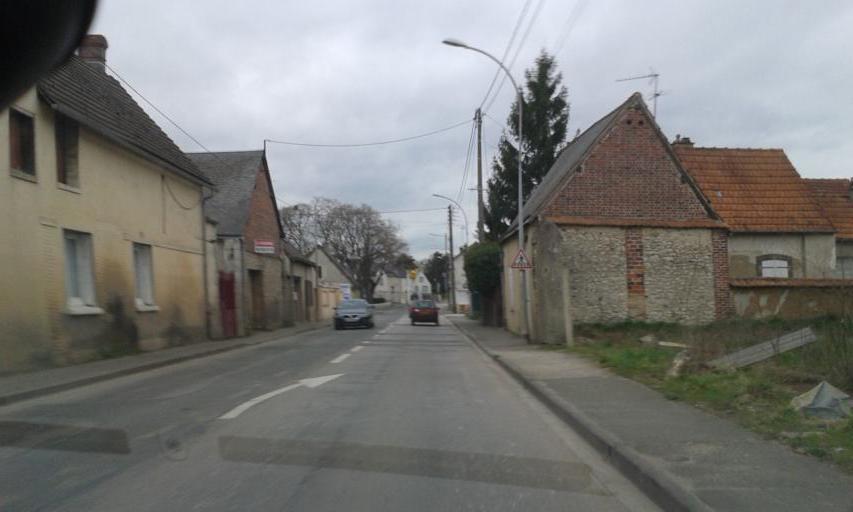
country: FR
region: Centre
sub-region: Departement d'Eure-et-Loir
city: Le Coudray
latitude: 48.4362
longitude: 1.5057
